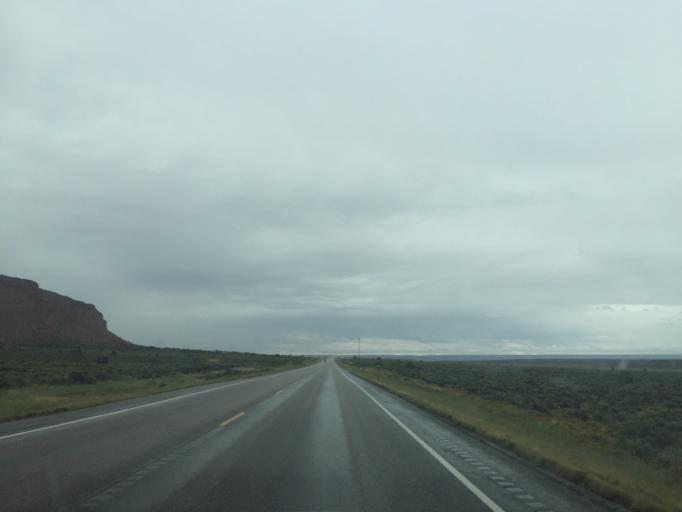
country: US
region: Utah
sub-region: Kane County
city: Kanab
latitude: 37.0257
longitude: -112.4652
